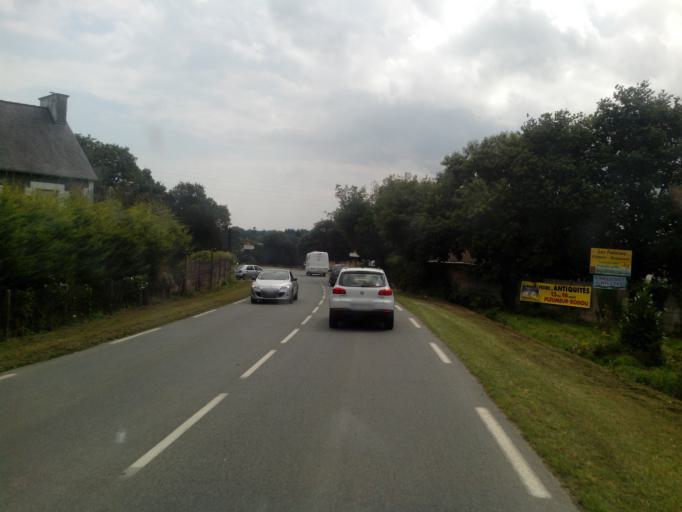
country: FR
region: Brittany
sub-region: Departement des Cotes-d'Armor
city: Plouha
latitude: 48.6708
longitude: -2.9309
